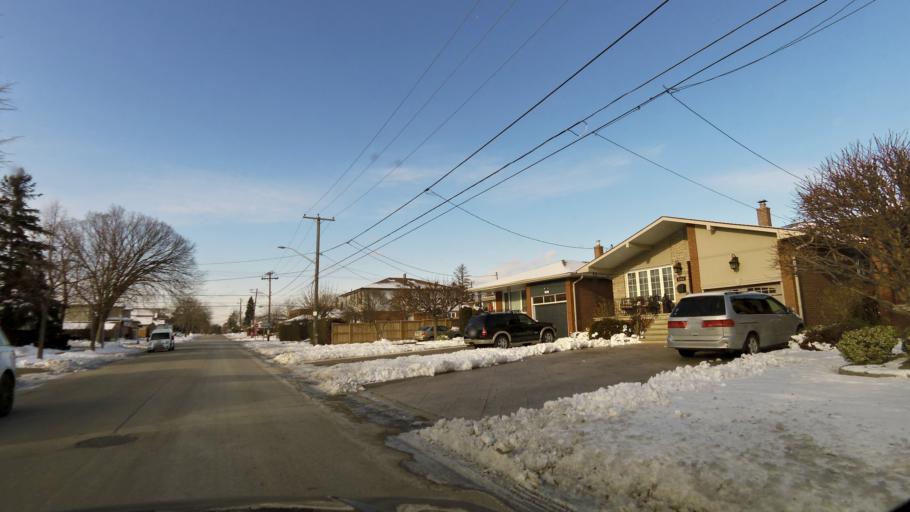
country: CA
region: Ontario
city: Etobicoke
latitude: 43.5791
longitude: -79.5669
